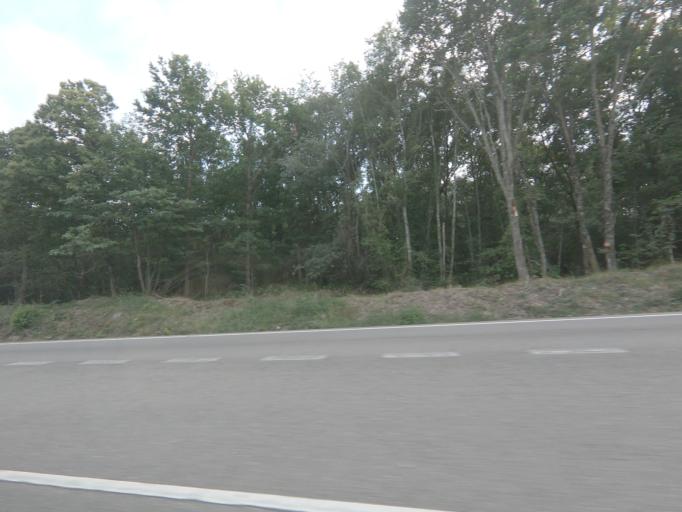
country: ES
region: Galicia
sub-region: Provincia de Ourense
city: Taboadela
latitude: 42.2199
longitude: -7.8409
